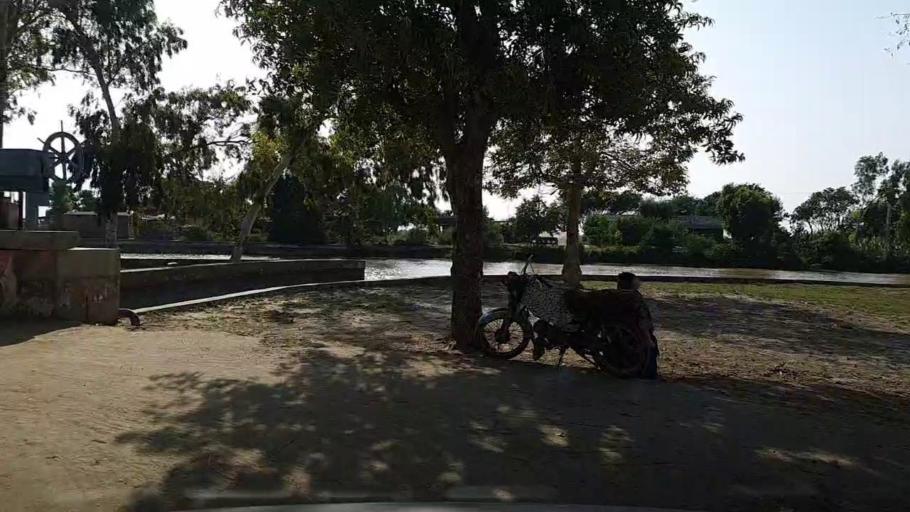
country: PK
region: Sindh
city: Kario
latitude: 24.8065
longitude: 68.5172
